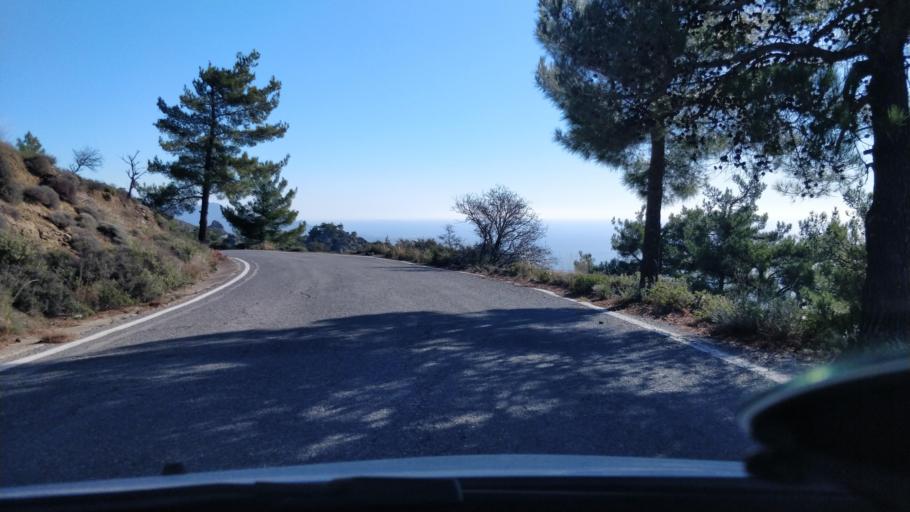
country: GR
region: Crete
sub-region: Nomos Lasithiou
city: Gra Liyia
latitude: 35.0439
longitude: 25.6337
